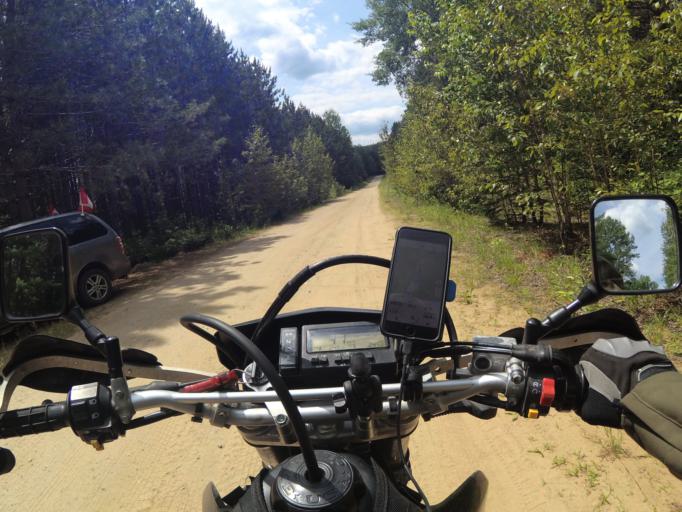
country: CA
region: Ontario
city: Bancroft
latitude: 45.0207
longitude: -77.2647
